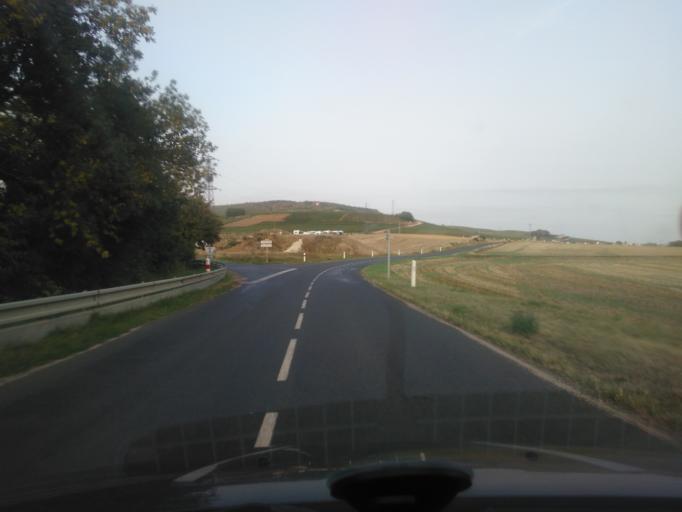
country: FR
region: Champagne-Ardenne
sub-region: Departement de la Marne
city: Mareuil-le-Port
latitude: 49.0882
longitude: 3.7790
